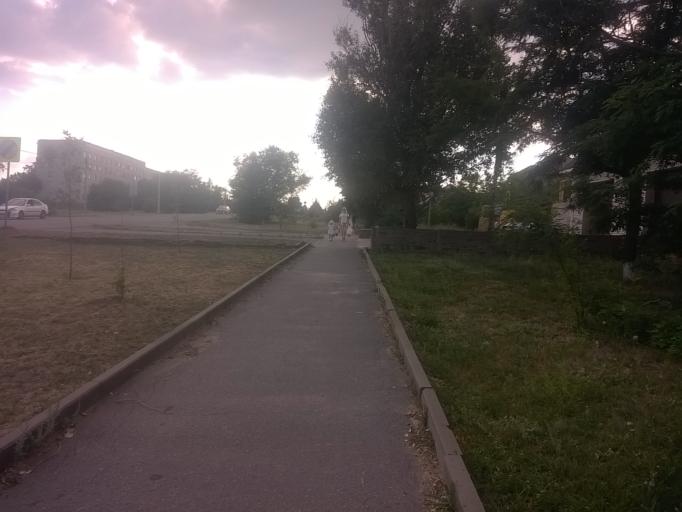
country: RU
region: Rostov
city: Donetsk
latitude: 48.3305
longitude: 39.9572
